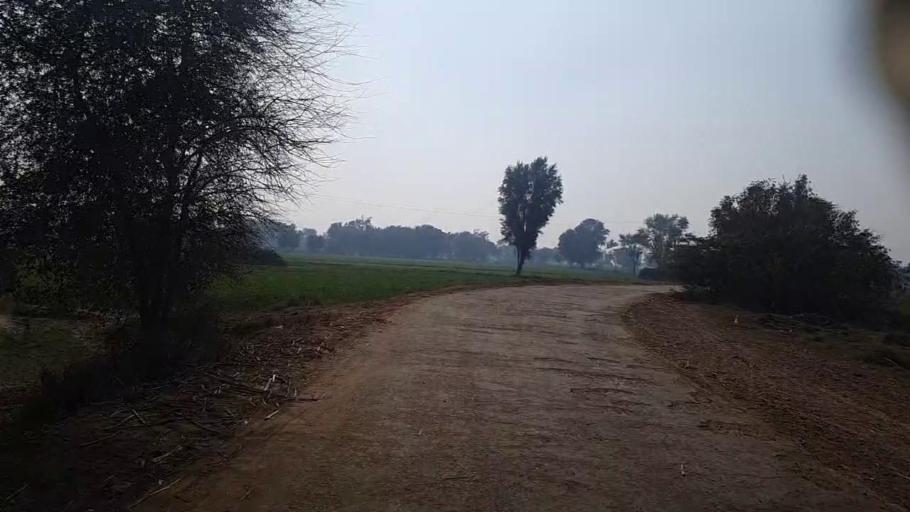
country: PK
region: Sindh
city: Khairpur
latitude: 27.9431
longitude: 69.6732
